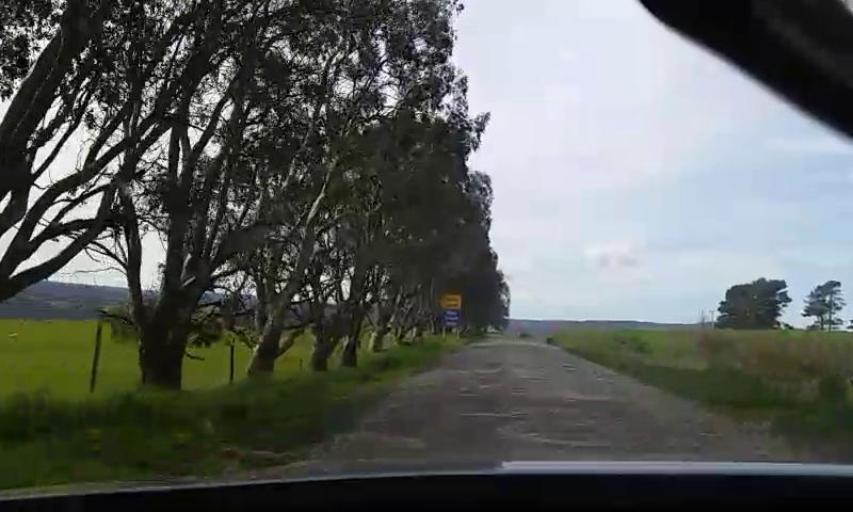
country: NZ
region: Otago
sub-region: Clutha District
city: Papatowai
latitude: -46.6317
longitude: 168.9775
